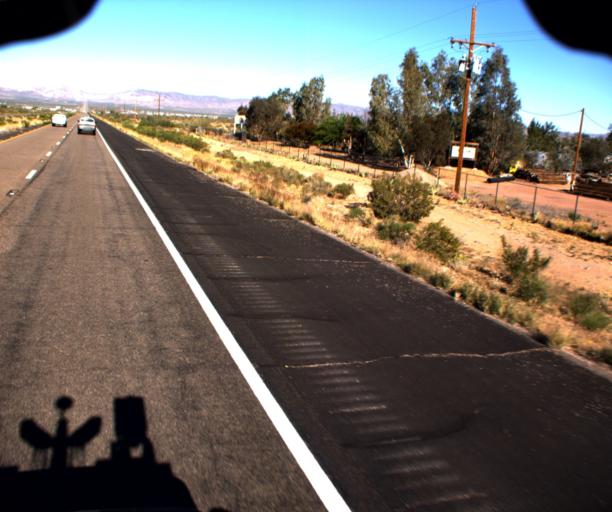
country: US
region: Arizona
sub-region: Mohave County
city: Golden Valley
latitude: 35.2236
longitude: -114.2457
